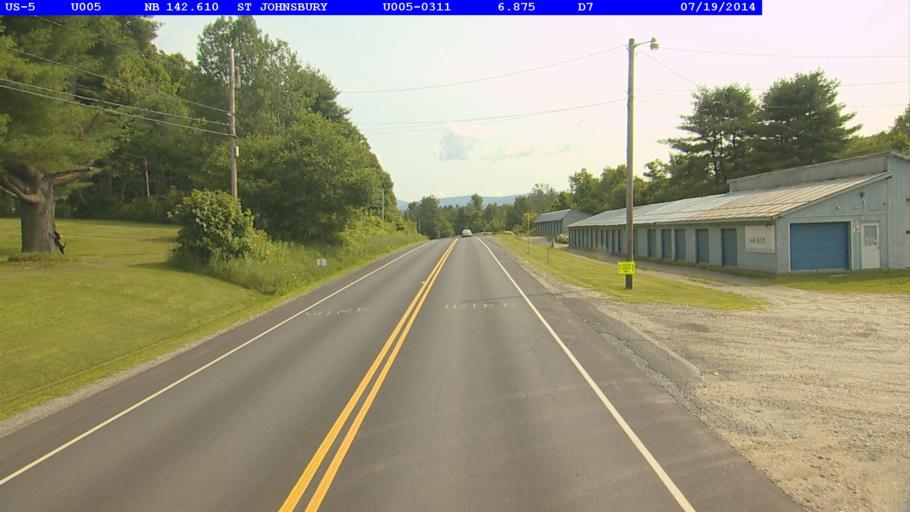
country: US
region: Vermont
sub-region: Caledonia County
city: Lyndon
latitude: 44.4879
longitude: -72.0086
